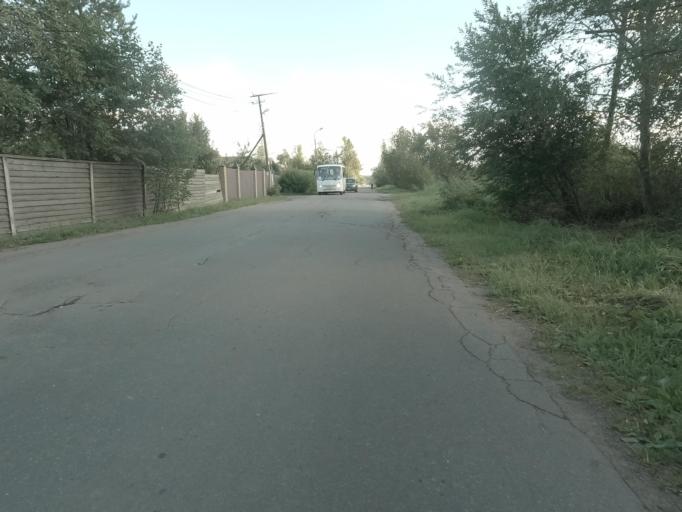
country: RU
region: Leningrad
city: Imeni Morozova
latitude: 59.9636
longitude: 31.0297
